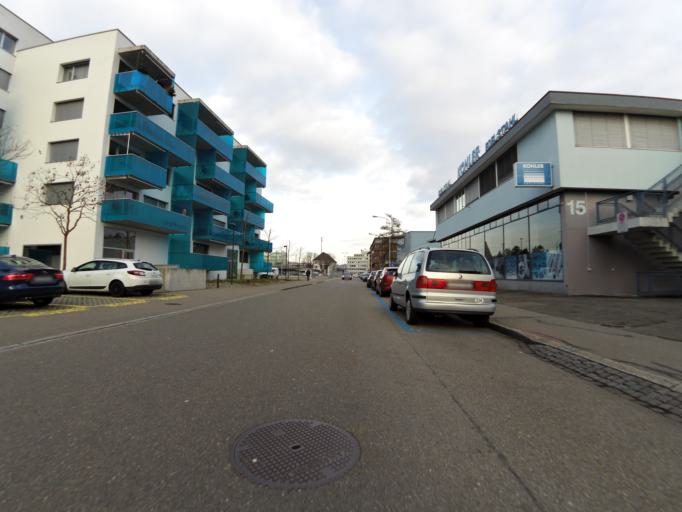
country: CH
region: Zurich
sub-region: Bezirk Dietikon
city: Schlieren / Zentrum
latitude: 47.3986
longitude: 8.4444
